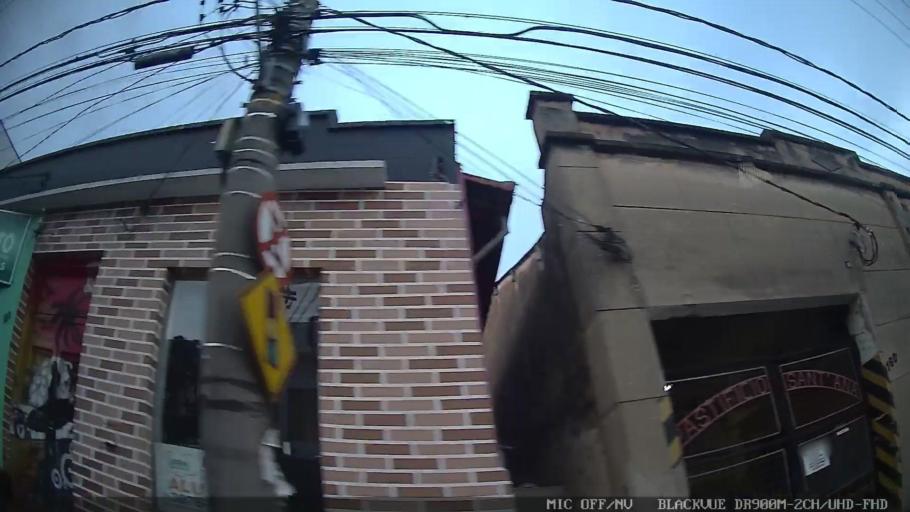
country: BR
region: Sao Paulo
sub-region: Vinhedo
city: Vinhedo
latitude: -23.0306
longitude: -46.9723
